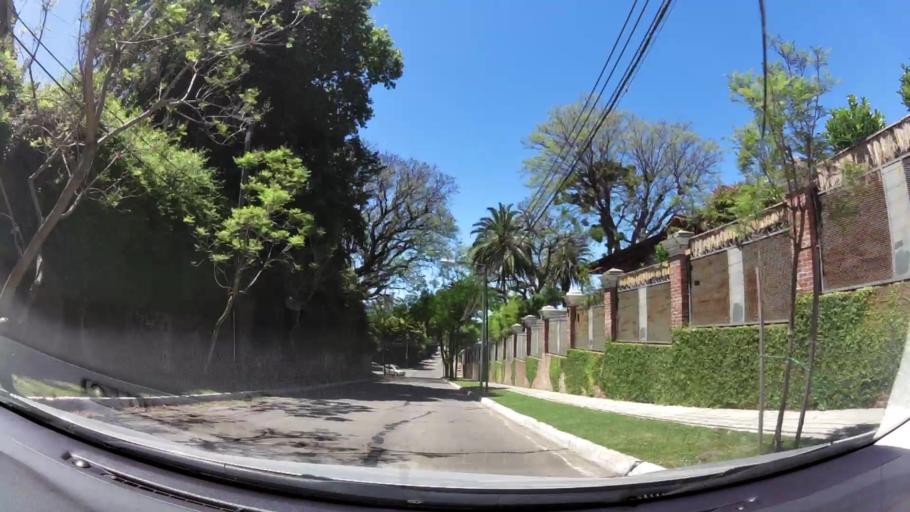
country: AR
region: Buenos Aires
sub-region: Partido de San Isidro
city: San Isidro
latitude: -34.4536
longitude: -58.5237
